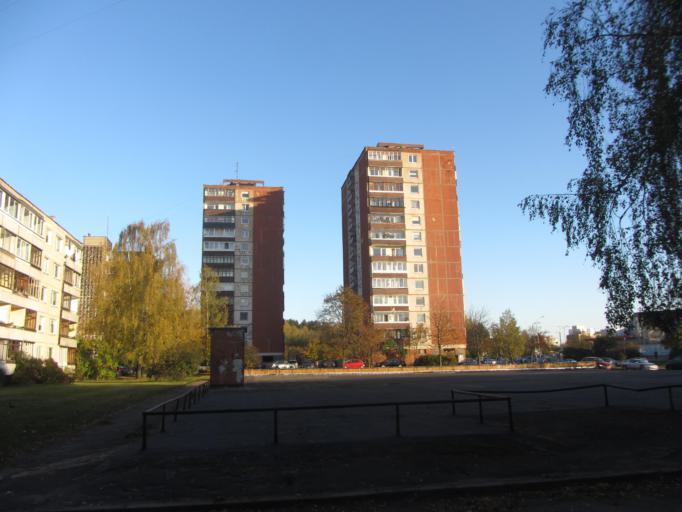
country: LT
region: Vilnius County
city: Lazdynai
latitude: 54.6863
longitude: 25.2033
